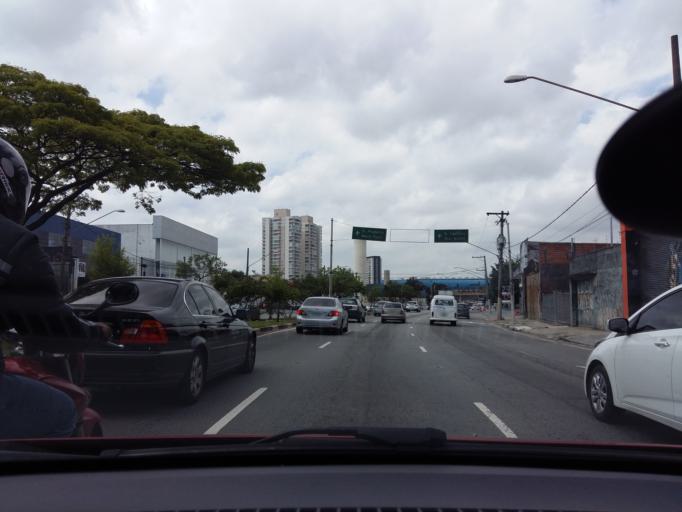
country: BR
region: Sao Paulo
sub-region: Sao Caetano Do Sul
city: Sao Caetano do Sul
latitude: -23.6064
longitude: -46.6053
